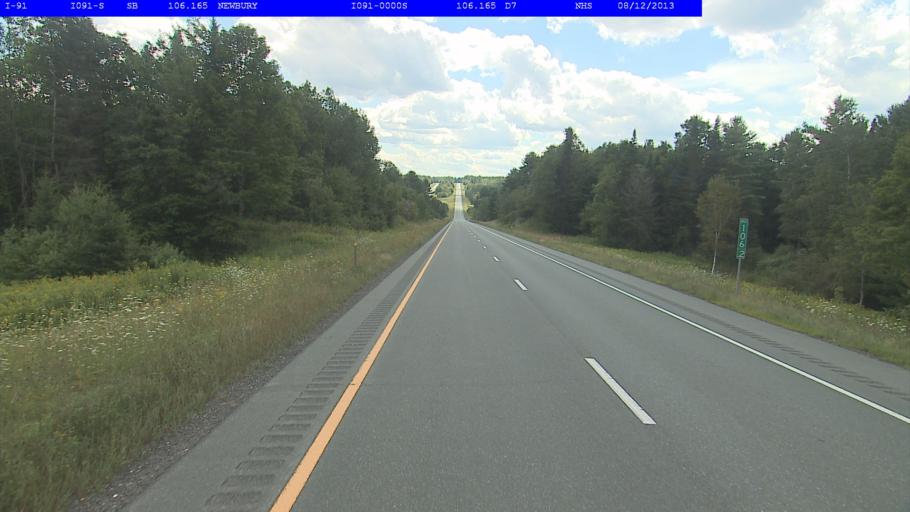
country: US
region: New Hampshire
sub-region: Grafton County
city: Haverhill
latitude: 44.1027
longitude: -72.1095
